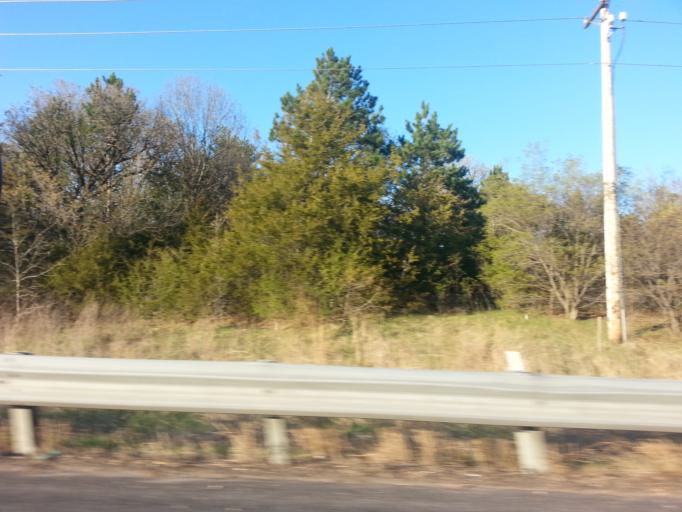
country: US
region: Wisconsin
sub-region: Pierce County
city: Prescott
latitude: 44.6609
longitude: -92.7741
